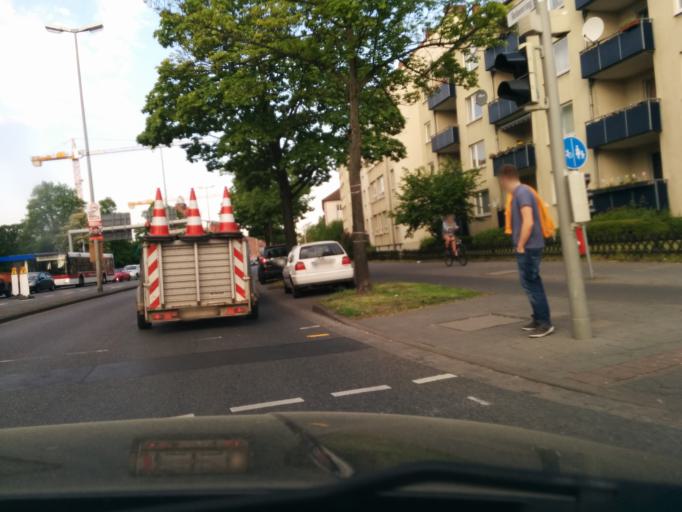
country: DE
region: Lower Saxony
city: Braunschweig
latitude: 52.2756
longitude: 10.5353
